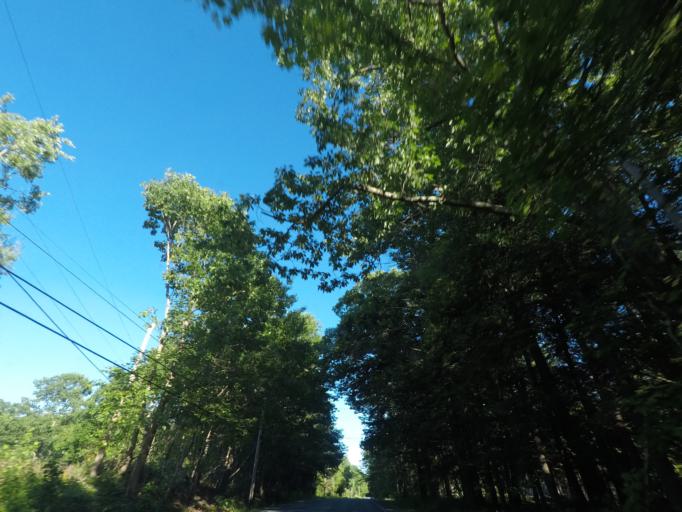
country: US
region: New York
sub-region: Rensselaer County
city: West Sand Lake
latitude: 42.5968
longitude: -73.5946
